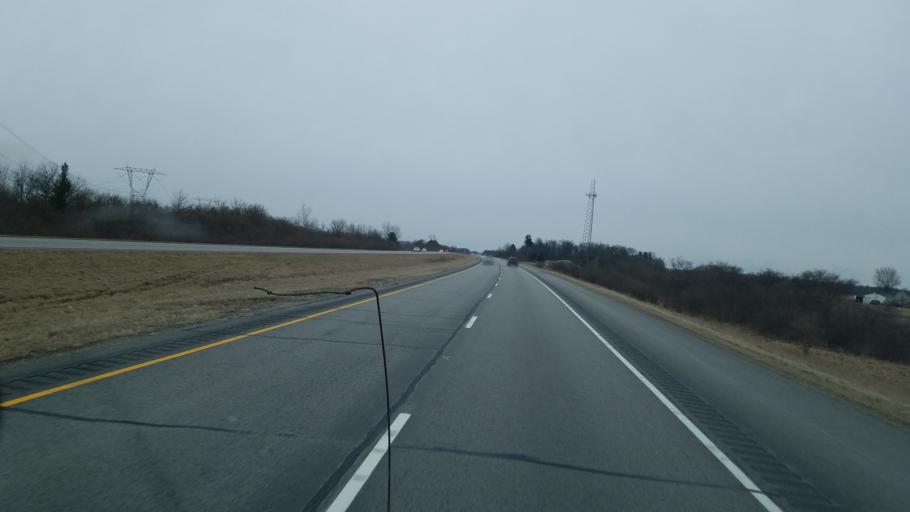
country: US
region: Indiana
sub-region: Marshall County
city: Argos
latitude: 41.2055
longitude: -86.2592
